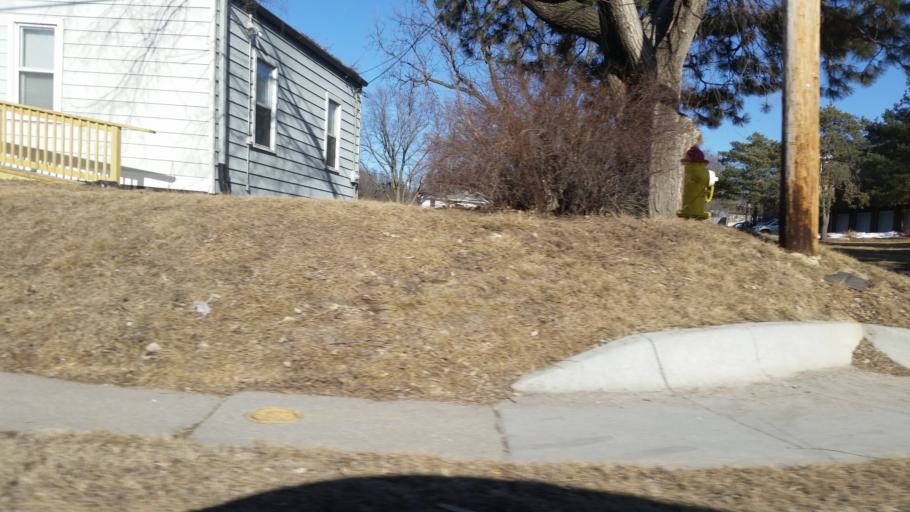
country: US
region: Nebraska
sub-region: Sarpy County
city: Bellevue
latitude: 41.1613
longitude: -95.9213
